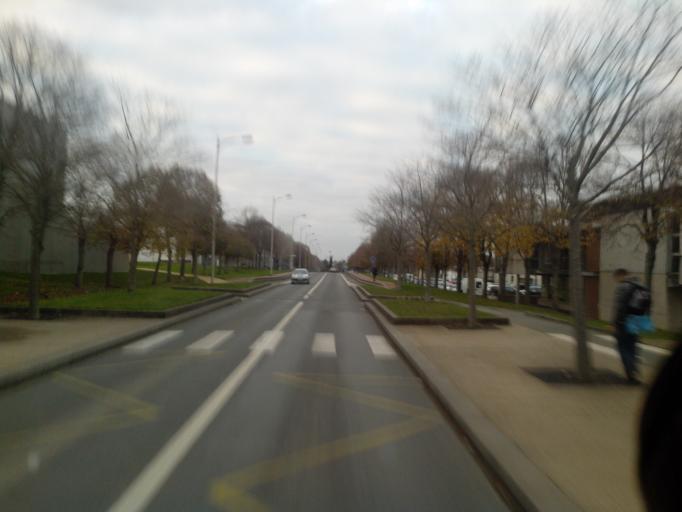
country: FR
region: Poitou-Charentes
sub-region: Departement de la Vienne
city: Mignaloux-Beauvoir
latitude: 46.5681
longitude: 0.3870
